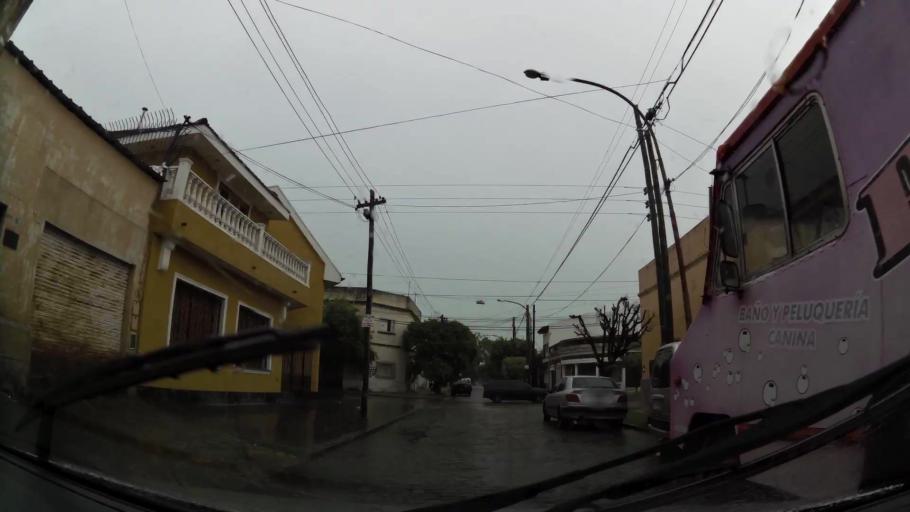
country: AR
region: Buenos Aires
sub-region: Partido de Lanus
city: Lanus
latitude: -34.7254
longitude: -58.4055
